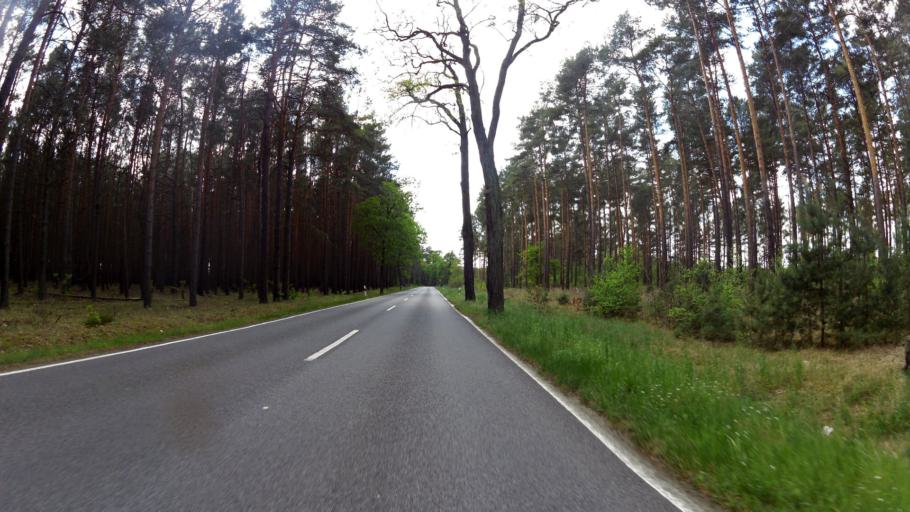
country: DE
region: Brandenburg
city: Gross Koris
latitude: 52.1730
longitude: 13.7128
